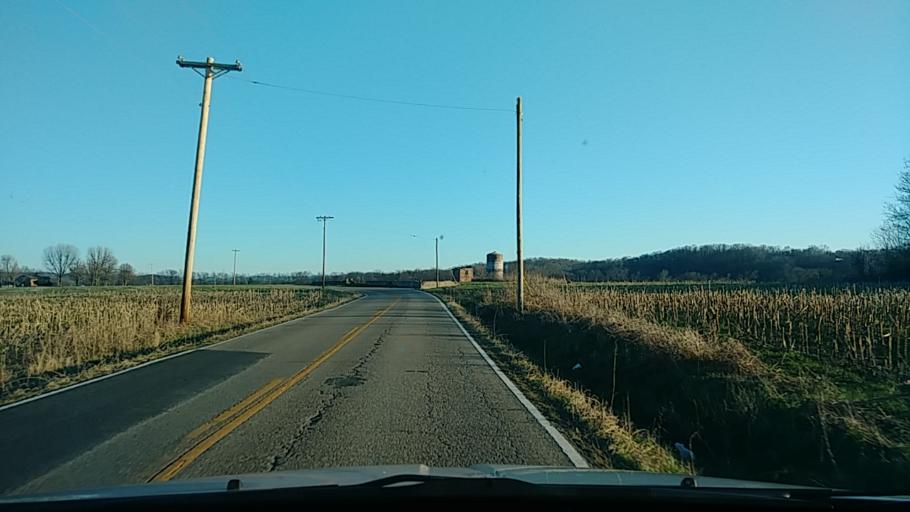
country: US
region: Tennessee
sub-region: Jefferson County
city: White Pine
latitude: 36.1538
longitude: -83.1592
